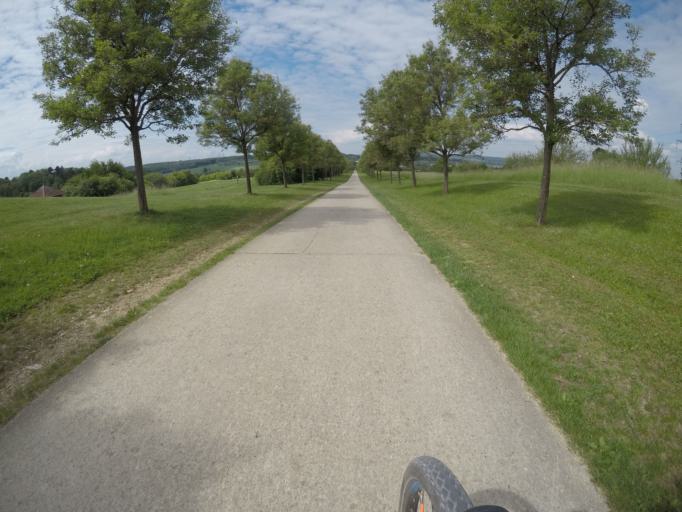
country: DE
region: Baden-Wuerttemberg
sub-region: Regierungsbezirk Stuttgart
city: Wernau
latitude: 48.6710
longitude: 9.4169
